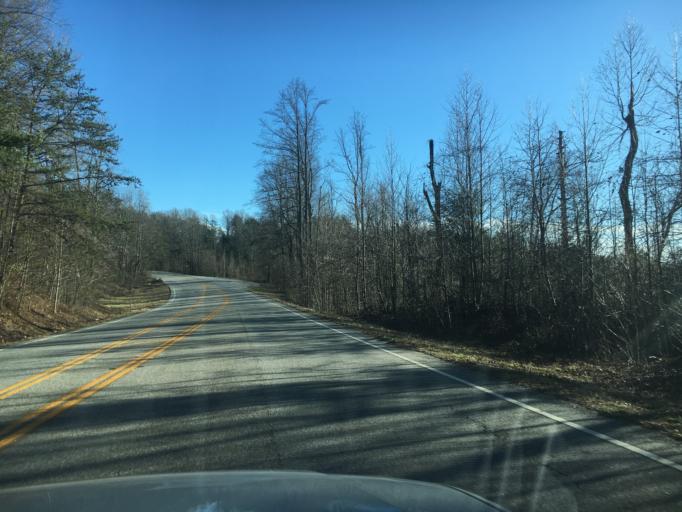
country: US
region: Georgia
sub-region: White County
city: Cleveland
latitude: 34.6886
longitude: -83.9082
